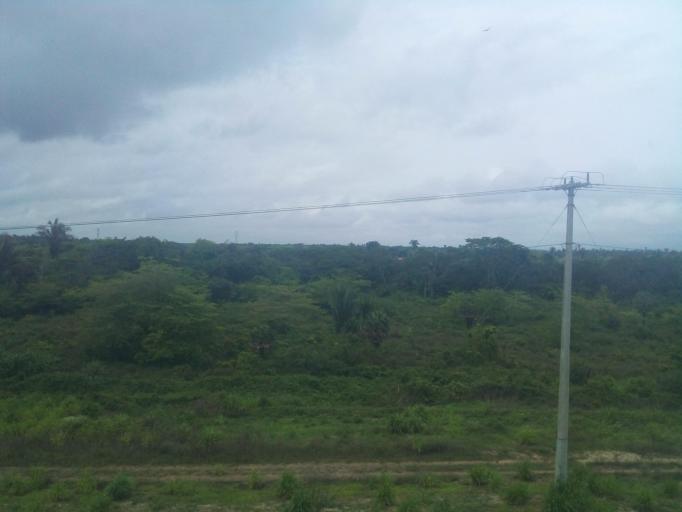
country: BR
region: Maranhao
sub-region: Vitoria Do Mearim
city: Vitoria do Mearim
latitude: -3.5479
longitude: -44.8304
